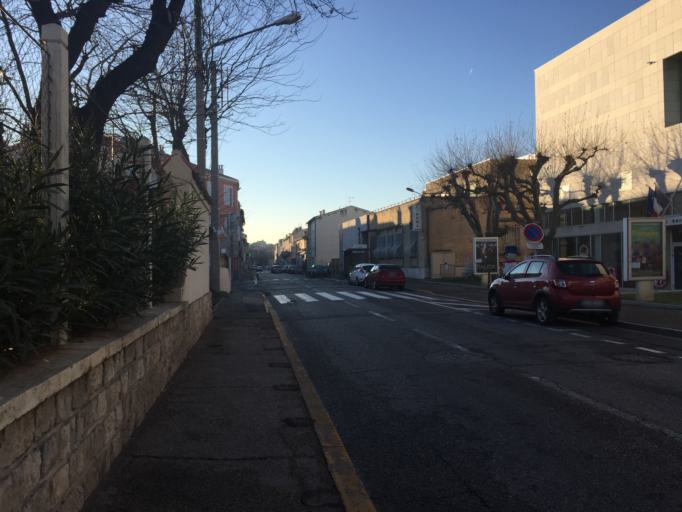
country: FR
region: Provence-Alpes-Cote d'Azur
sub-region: Departement des Bouches-du-Rhone
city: Marignane
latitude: 43.4196
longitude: 5.2138
